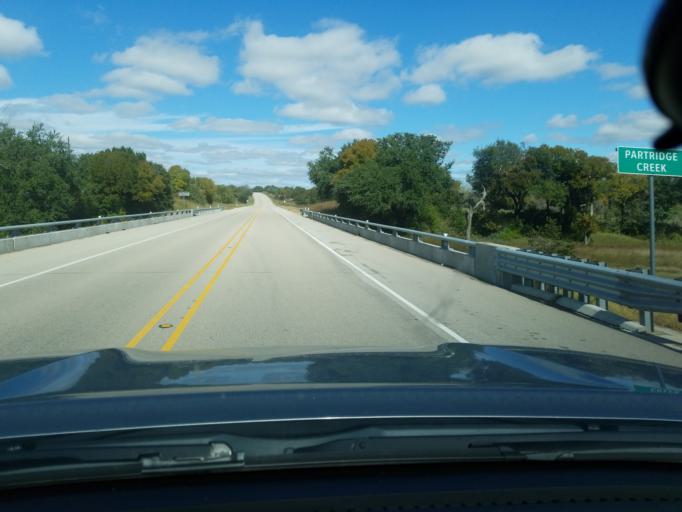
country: US
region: Texas
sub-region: Hamilton County
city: Hamilton
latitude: 31.5819
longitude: -98.1571
